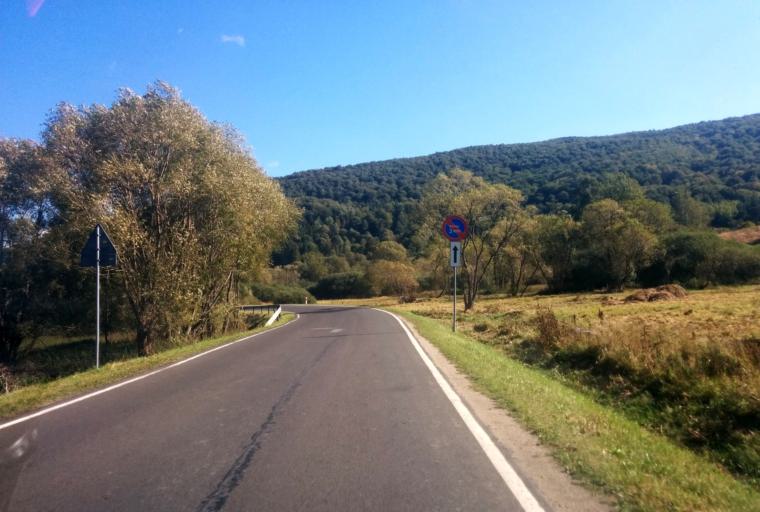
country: PL
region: Subcarpathian Voivodeship
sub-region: Powiat bieszczadzki
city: Lutowiska
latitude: 49.1091
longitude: 22.6563
